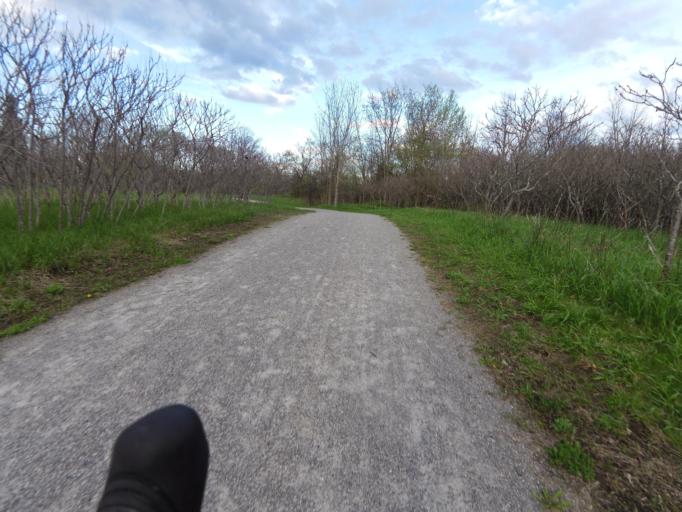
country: CA
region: Ontario
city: Ottawa
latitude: 45.3165
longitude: -75.7153
